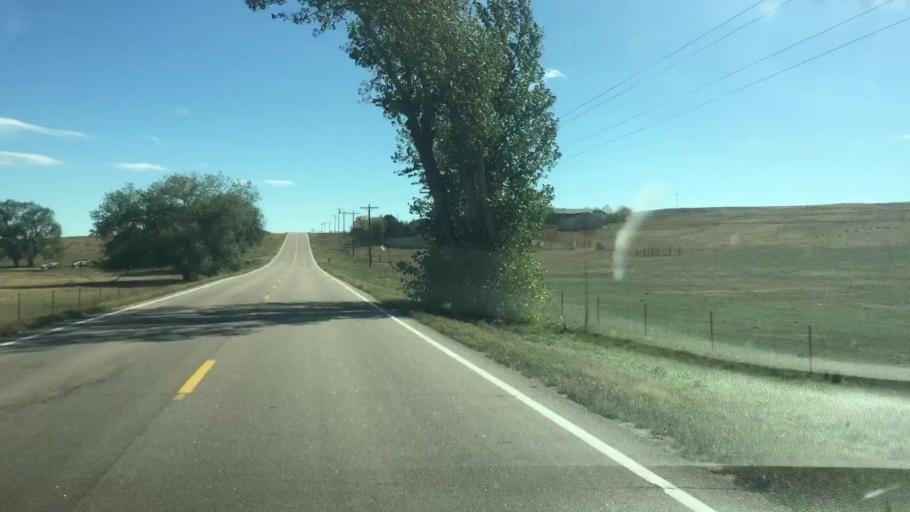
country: US
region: Colorado
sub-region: Elbert County
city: Kiowa
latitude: 39.2736
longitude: -104.1343
